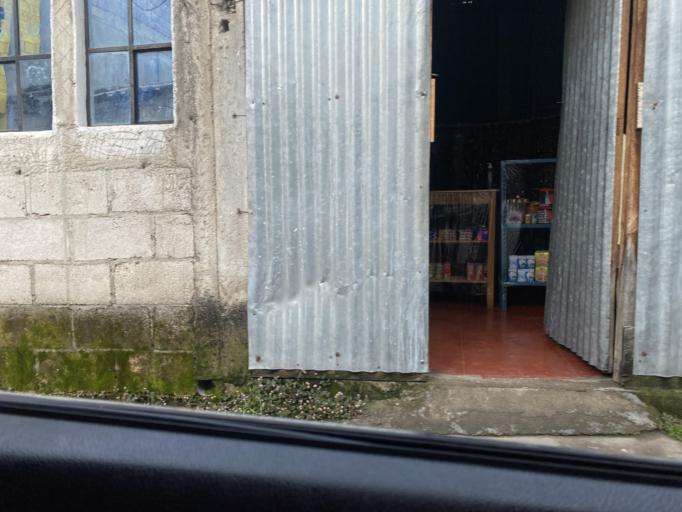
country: GT
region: Quetzaltenango
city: Olintepeque
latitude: 14.8610
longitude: -91.5187
